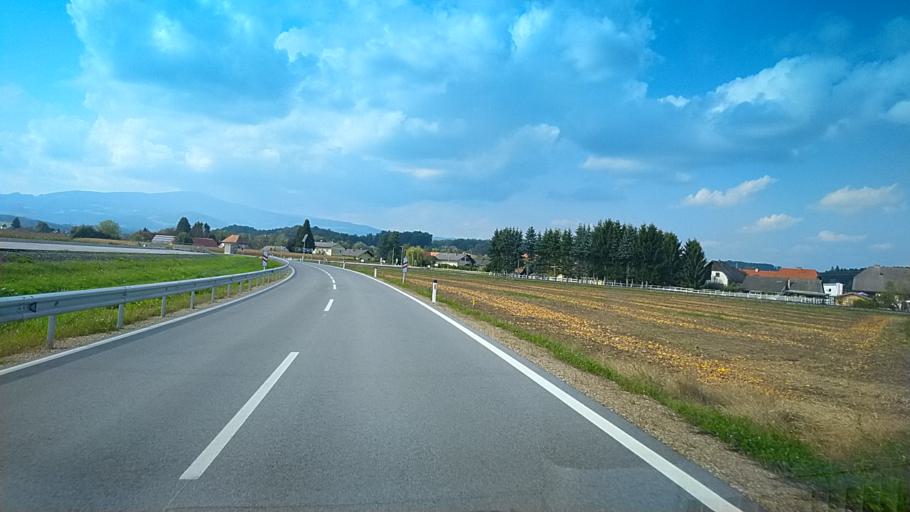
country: AT
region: Styria
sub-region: Politischer Bezirk Deutschlandsberg
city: Gross Sankt Florian
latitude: 46.8210
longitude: 15.2832
